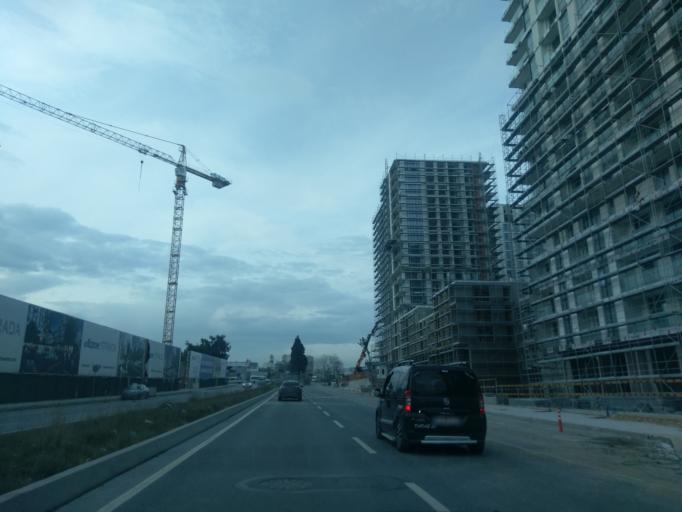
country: TR
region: Istanbul
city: Esenyurt
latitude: 41.0748
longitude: 28.6573
